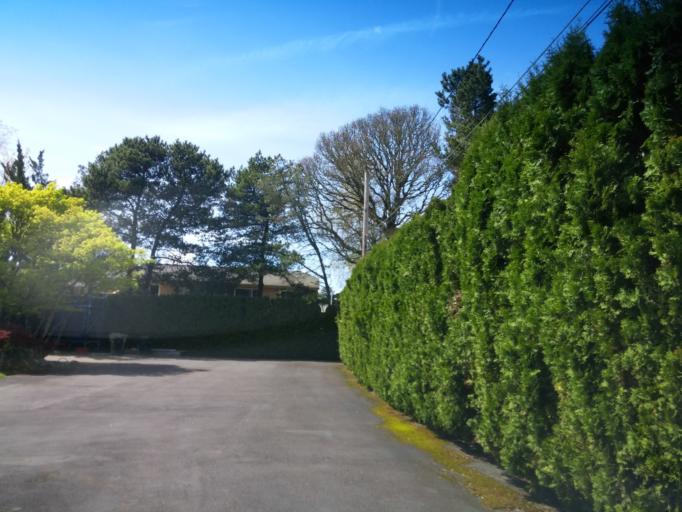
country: US
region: Oregon
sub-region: Washington County
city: Cedar Mill
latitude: 45.5248
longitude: -122.8041
